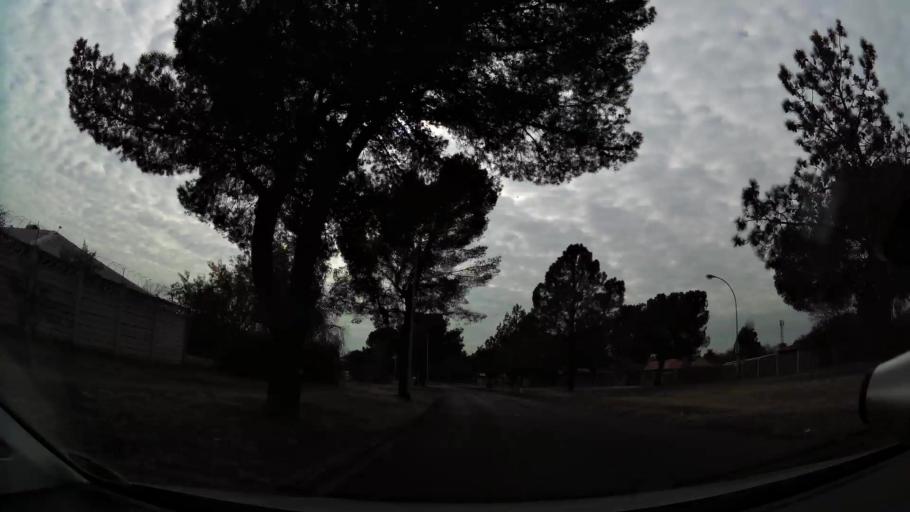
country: ZA
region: Orange Free State
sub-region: Mangaung Metropolitan Municipality
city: Bloemfontein
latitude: -29.1296
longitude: 26.2010
